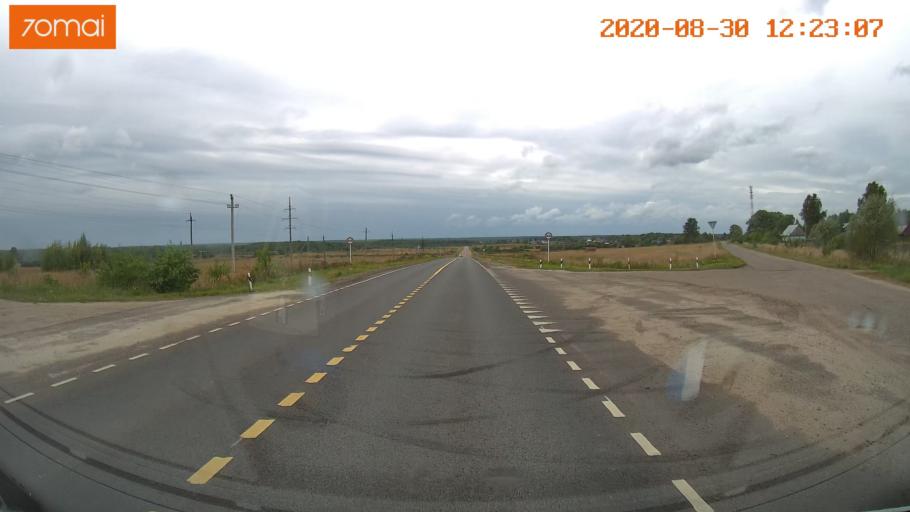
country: RU
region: Ivanovo
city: Yur'yevets
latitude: 57.3311
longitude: 42.8323
